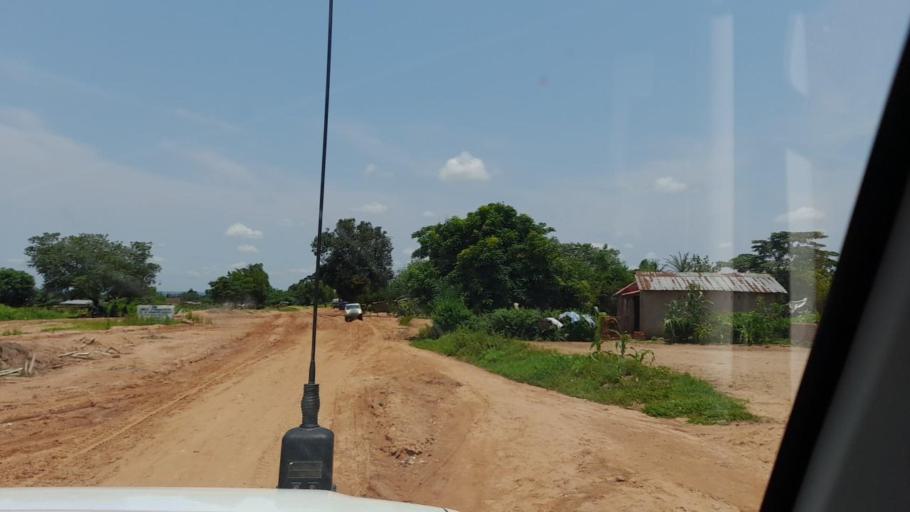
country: CD
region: Kasai-Occidental
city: Kananga
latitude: -5.9507
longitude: 22.2775
